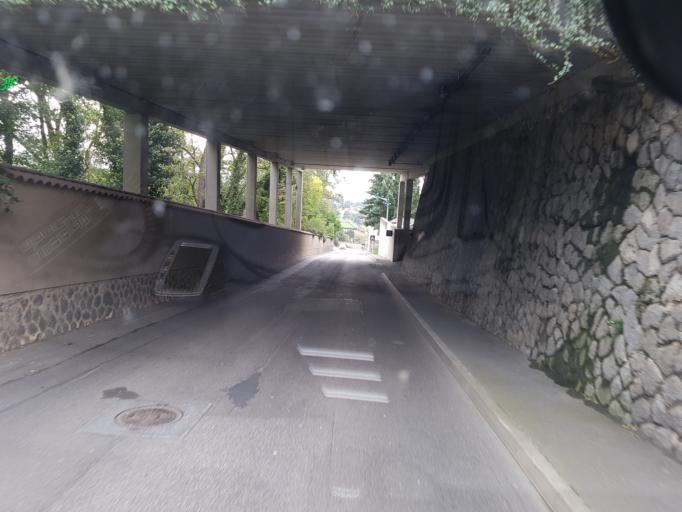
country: FR
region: Rhone-Alpes
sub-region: Departement de la Loire
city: Saint-Galmier
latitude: 45.5908
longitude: 4.3198
